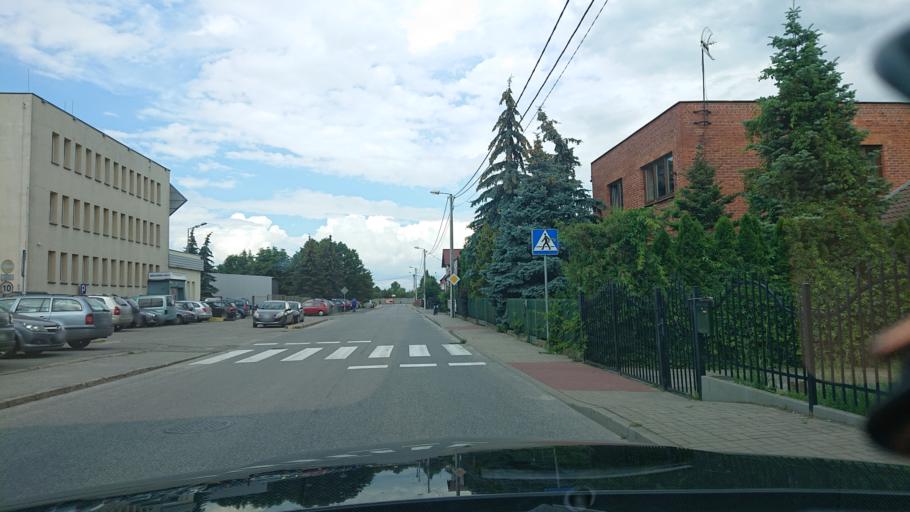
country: PL
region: Greater Poland Voivodeship
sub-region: Powiat gnieznienski
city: Gniezno
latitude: 52.5399
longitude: 17.6341
